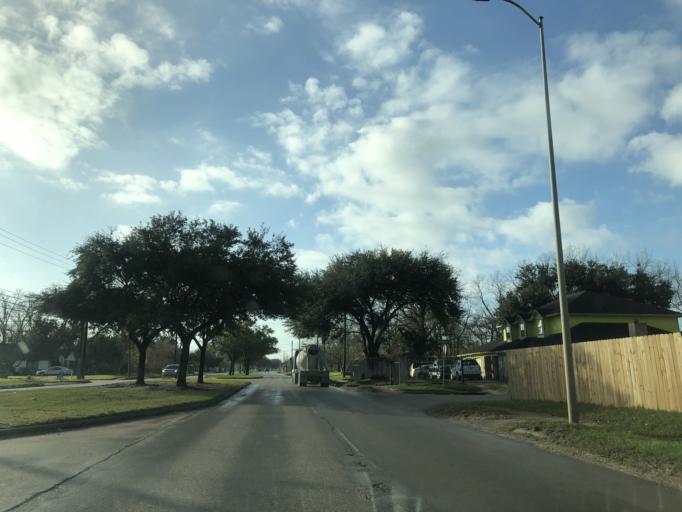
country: US
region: Texas
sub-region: Harris County
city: Jacinto City
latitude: 29.8250
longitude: -95.2845
